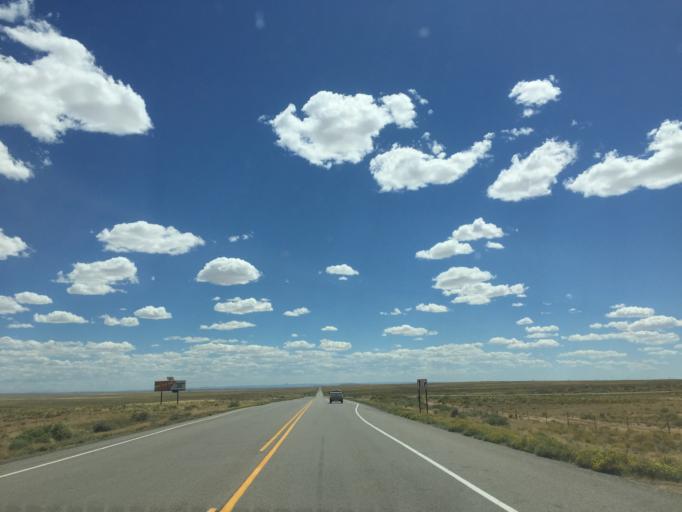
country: US
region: New Mexico
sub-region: San Juan County
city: Upper Fruitland
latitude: 36.4398
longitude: -108.2518
